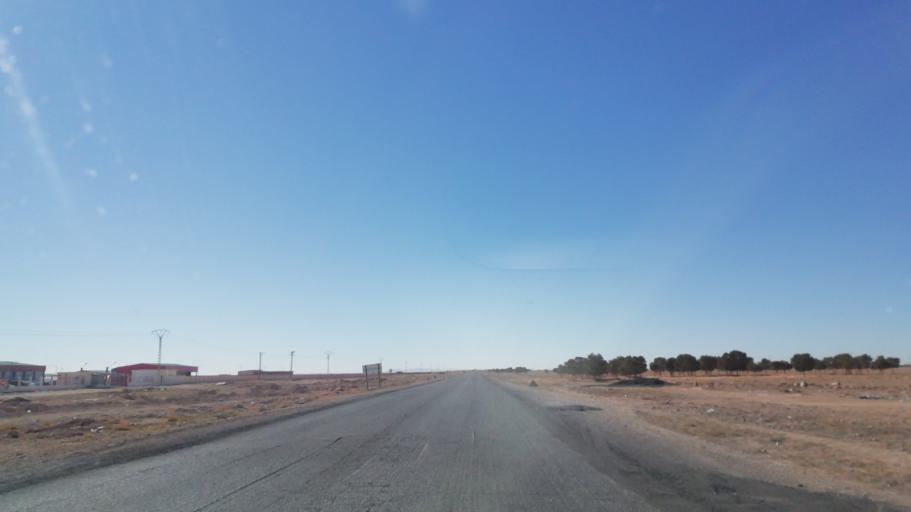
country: DZ
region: Saida
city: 'Ain el Hadjar
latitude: 34.0234
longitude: 0.0668
